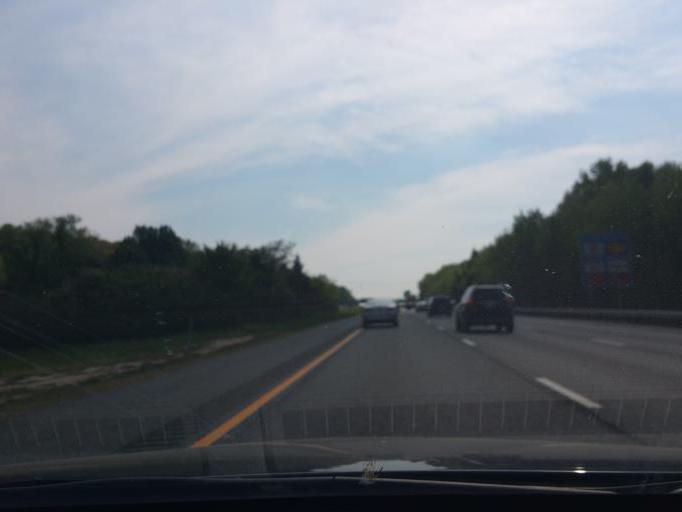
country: US
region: Maryland
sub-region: Harford County
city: Riverside
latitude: 39.4693
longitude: -76.2805
